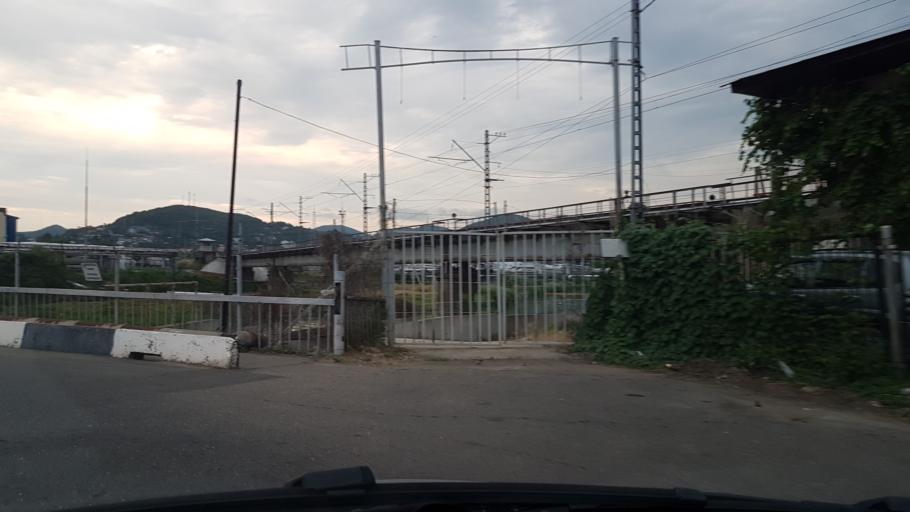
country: RU
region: Krasnodarskiy
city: Tuapse
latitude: 44.0899
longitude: 39.0827
